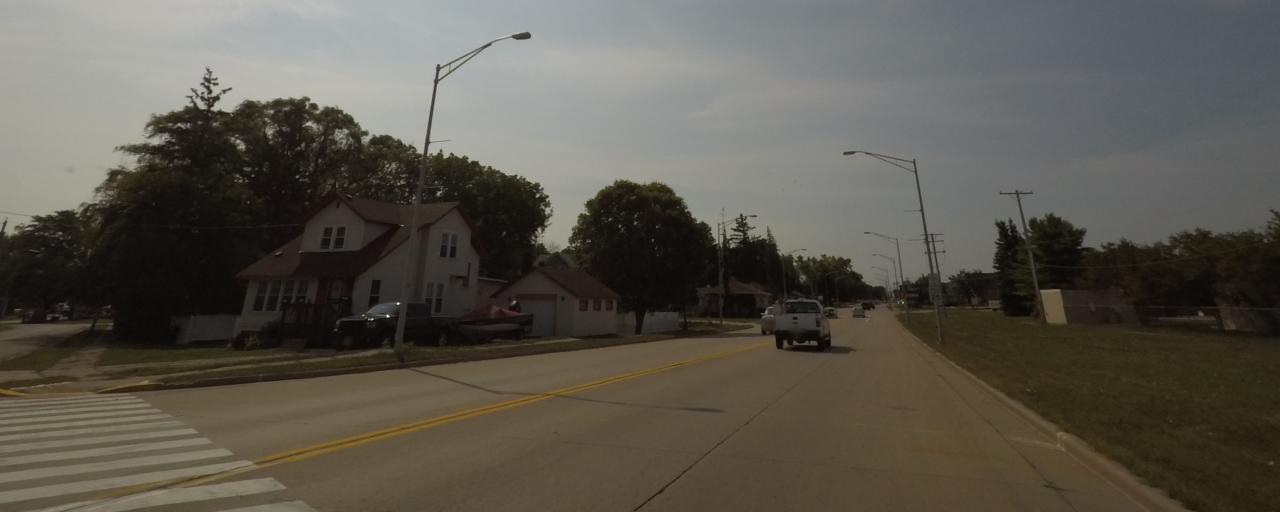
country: US
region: Wisconsin
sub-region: Jefferson County
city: Jefferson
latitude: 42.9961
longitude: -88.8075
